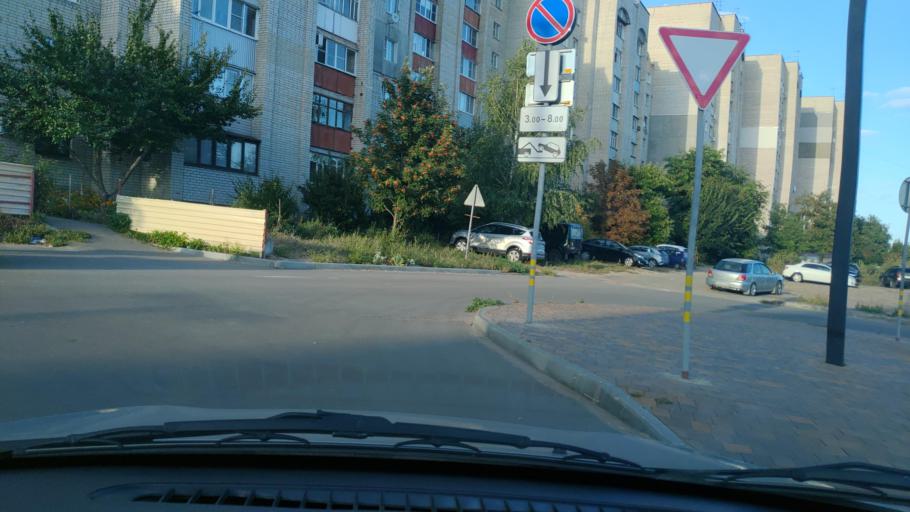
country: RU
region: Tambov
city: Tambov
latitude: 52.7296
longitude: 41.4566
